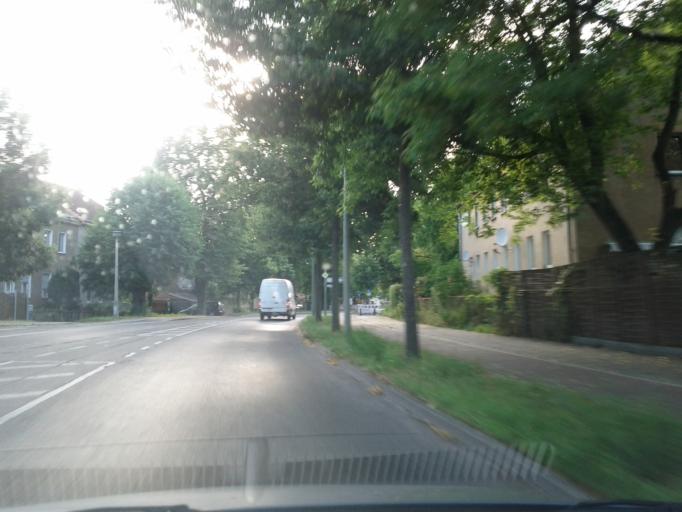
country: DE
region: Berlin
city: Falkenberg
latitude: 52.5679
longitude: 13.5450
